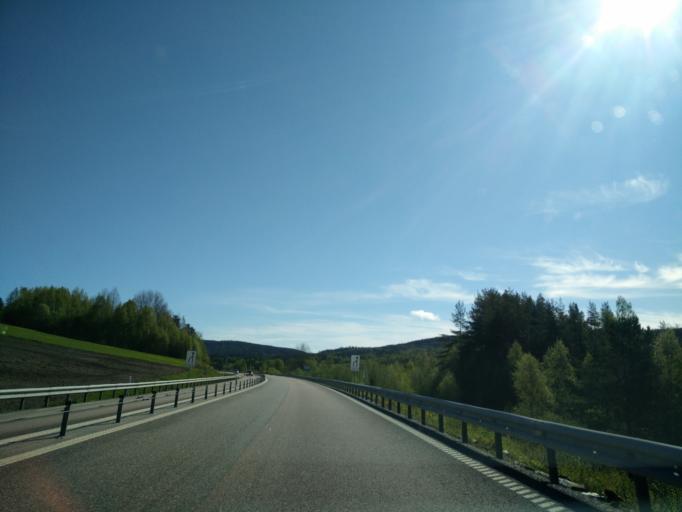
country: SE
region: Vaesternorrland
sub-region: Kramfors Kommun
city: Nordingra
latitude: 62.9613
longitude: 18.1398
